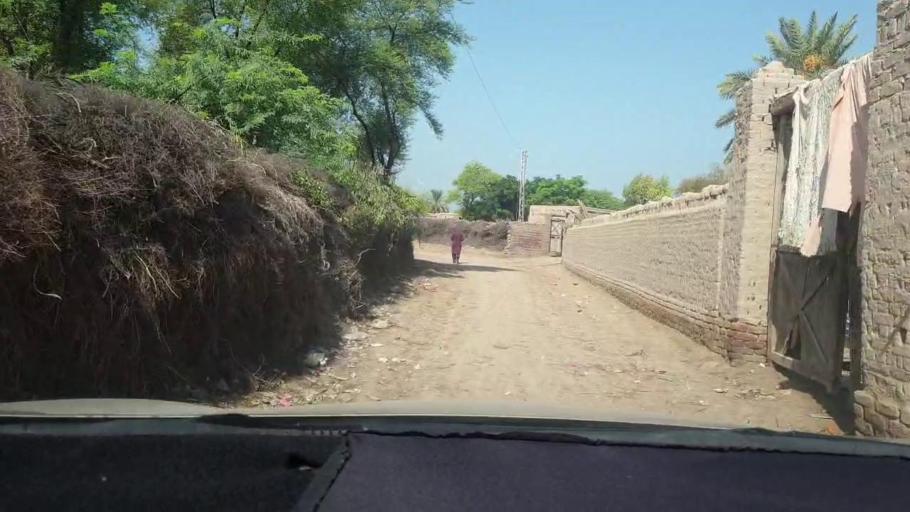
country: PK
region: Sindh
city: Miro Khan
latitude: 27.7059
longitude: 68.0947
